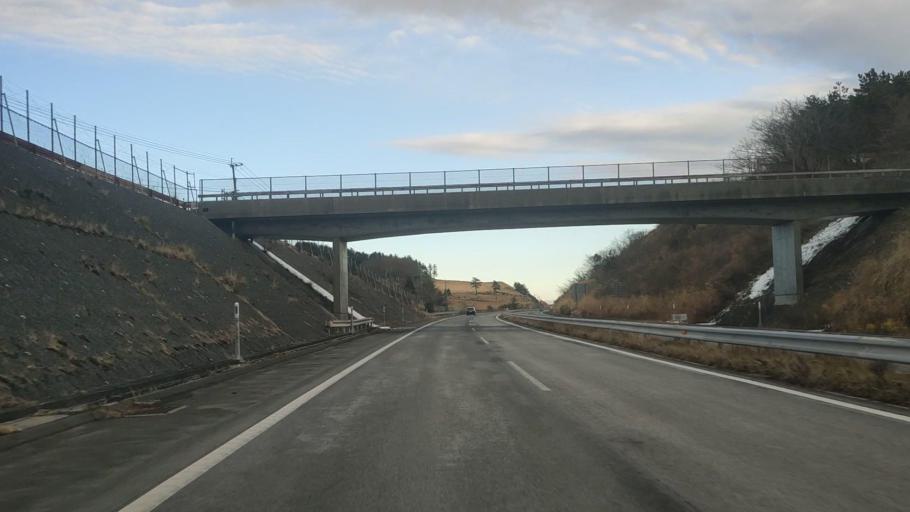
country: JP
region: Oita
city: Beppu
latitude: 33.3142
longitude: 131.4086
